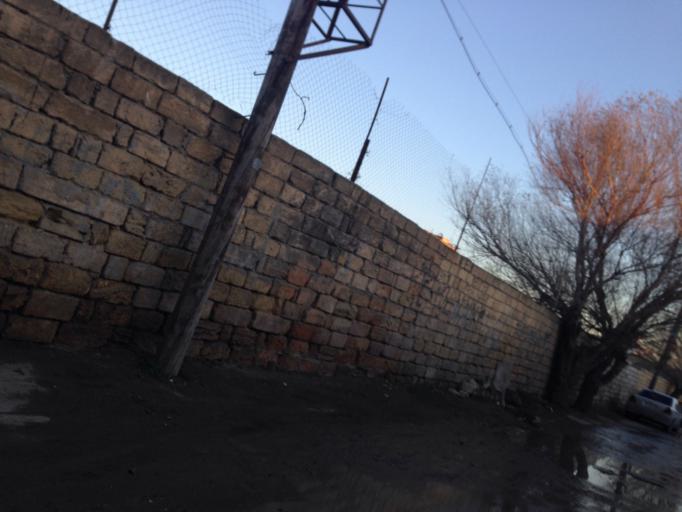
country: AZ
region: Baki
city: Baku
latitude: 40.4137
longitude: 49.8647
